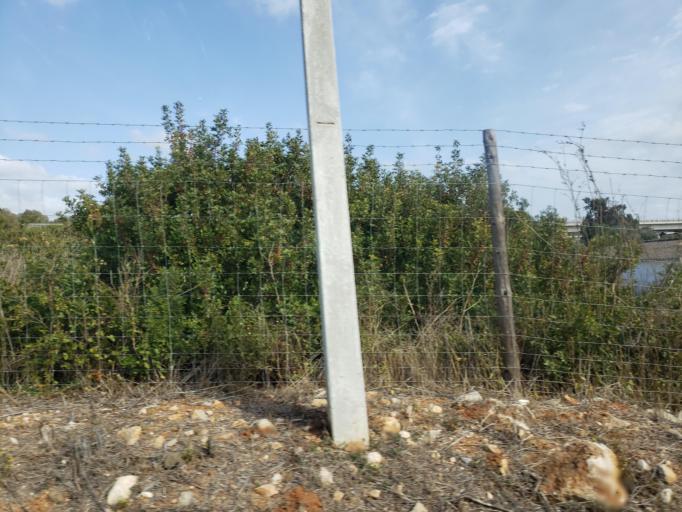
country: PT
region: Faro
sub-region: Portimao
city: Alvor
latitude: 37.1778
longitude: -8.5806
